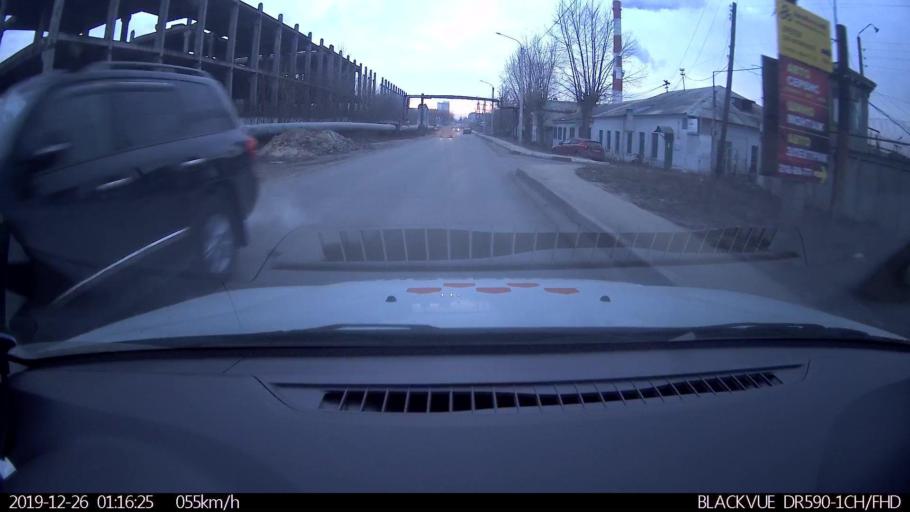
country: RU
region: Nizjnij Novgorod
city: Nizhniy Novgorod
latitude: 56.2696
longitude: 43.9069
